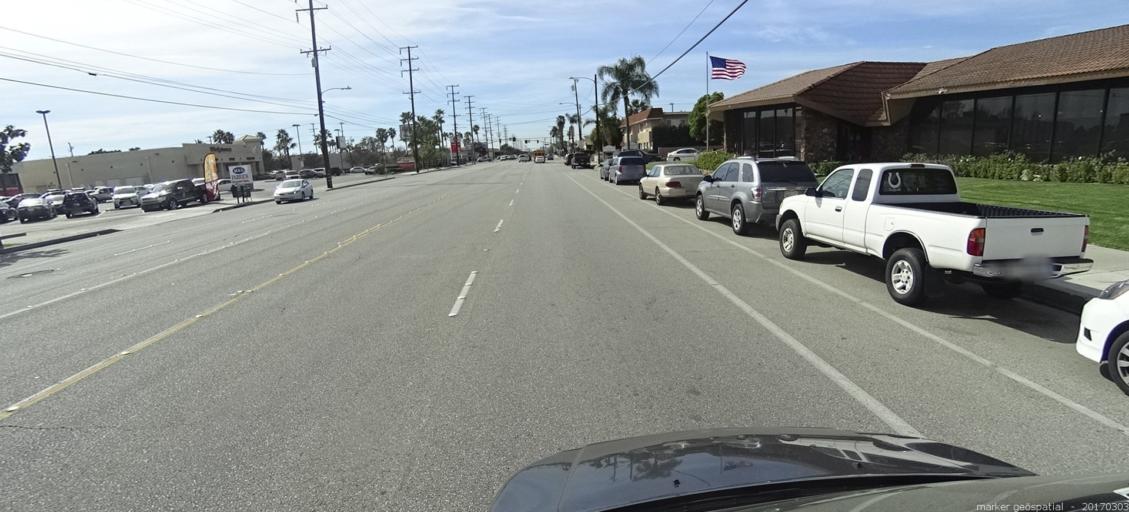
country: US
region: California
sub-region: Orange County
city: Stanton
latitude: 33.8173
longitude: -118.0085
